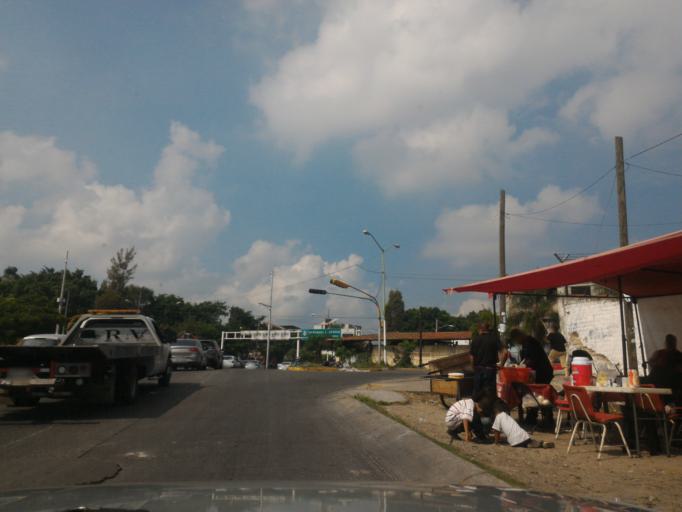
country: MX
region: Jalisco
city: Guadalajara
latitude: 20.6287
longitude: -103.4017
